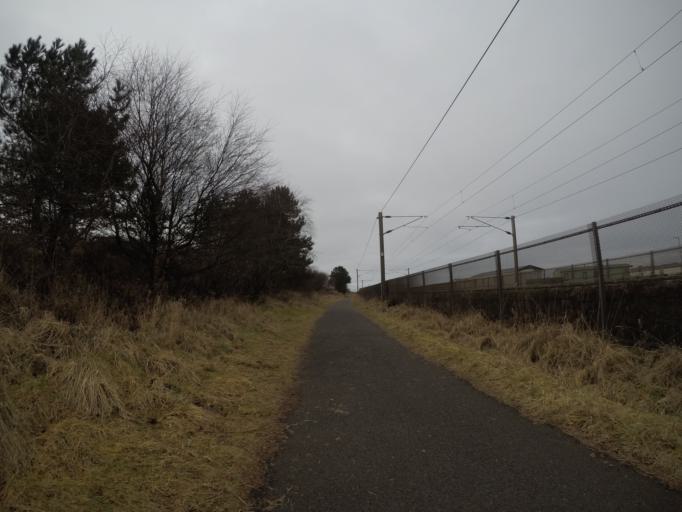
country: GB
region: Scotland
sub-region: North Ayrshire
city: Stevenston
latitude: 55.6324
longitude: -4.7596
